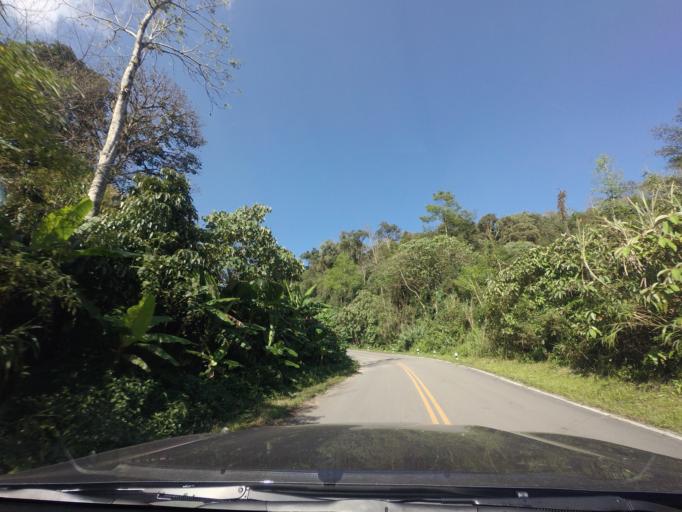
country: TH
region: Phetchabun
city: Lom Kao
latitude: 16.9032
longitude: 101.0740
